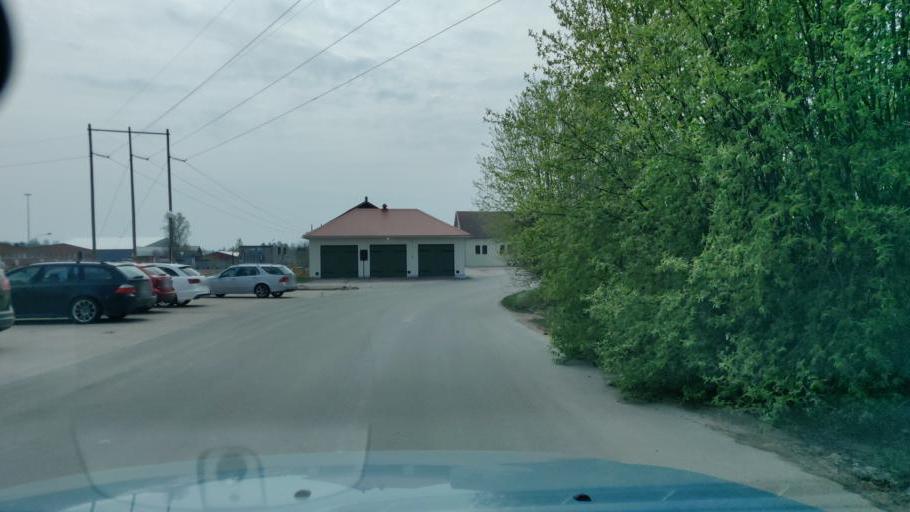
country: SE
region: Vaermland
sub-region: Munkfors Kommun
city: Munkfors
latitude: 59.8448
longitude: 13.5484
